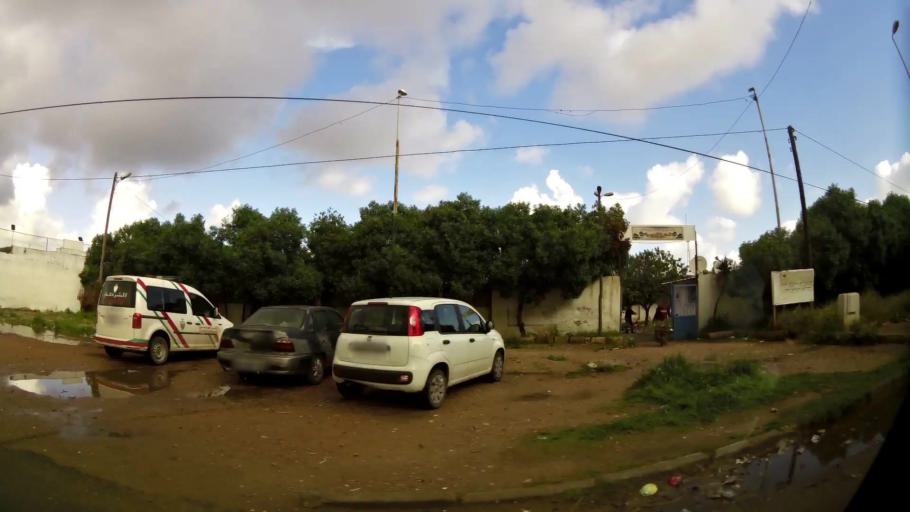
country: MA
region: Grand Casablanca
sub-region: Mediouna
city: Tit Mellil
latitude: 33.5934
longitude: -7.5214
